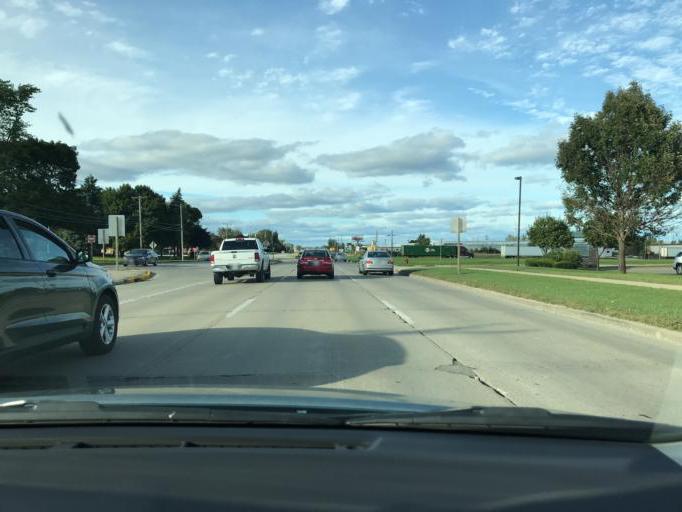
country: US
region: Wisconsin
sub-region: Kenosha County
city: Somers
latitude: 42.5905
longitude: -87.8818
